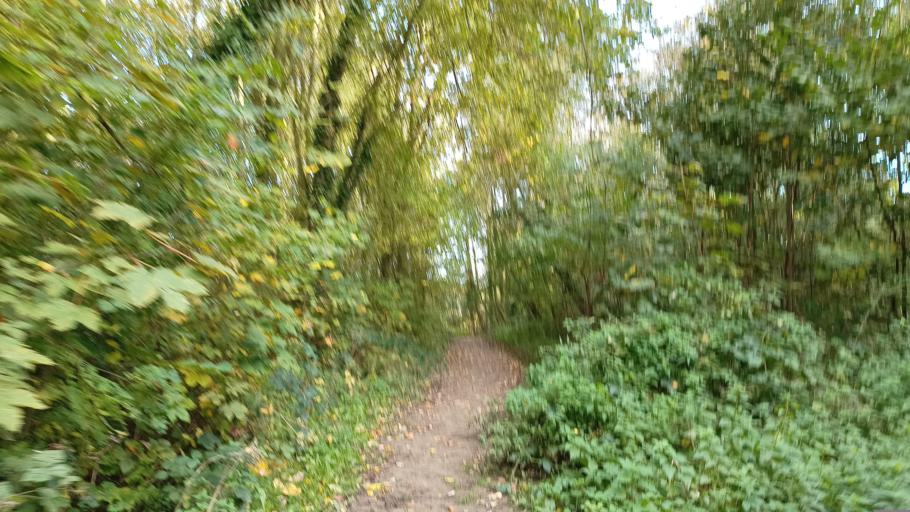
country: FR
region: Nord-Pas-de-Calais
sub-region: Departement du Nord
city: Nieppe
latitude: 50.7824
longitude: 2.8174
